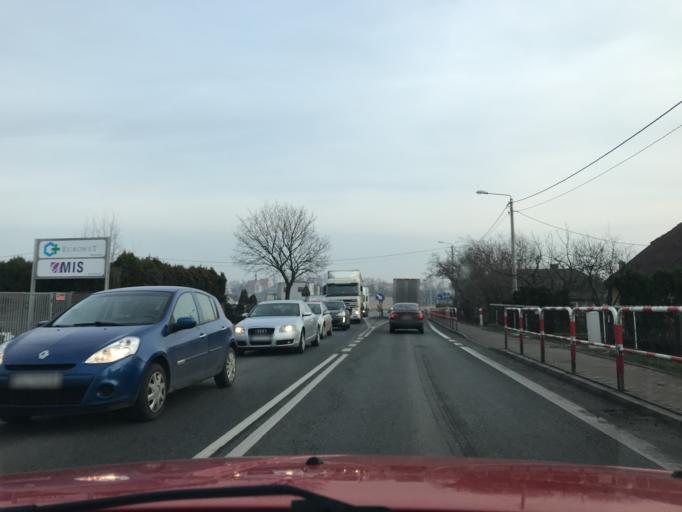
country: PL
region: Greater Poland Voivodeship
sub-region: Powiat ostrowski
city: Nowe Skalmierzyce
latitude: 51.7880
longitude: 18.0056
